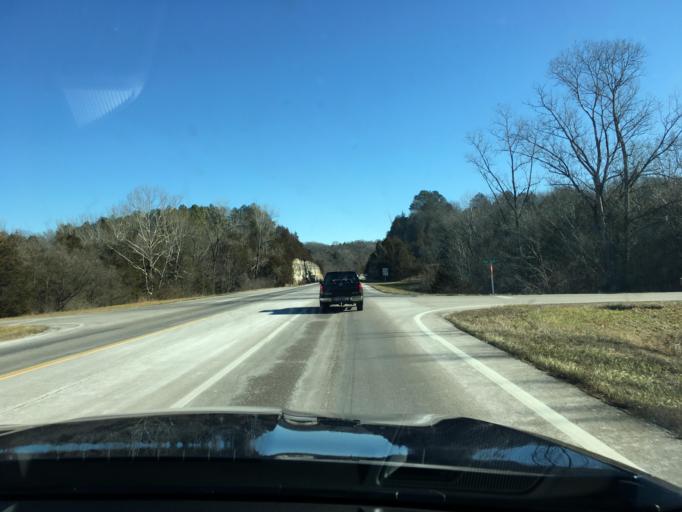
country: US
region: Missouri
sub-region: Jefferson County
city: De Soto
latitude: 38.1386
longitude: -90.4923
